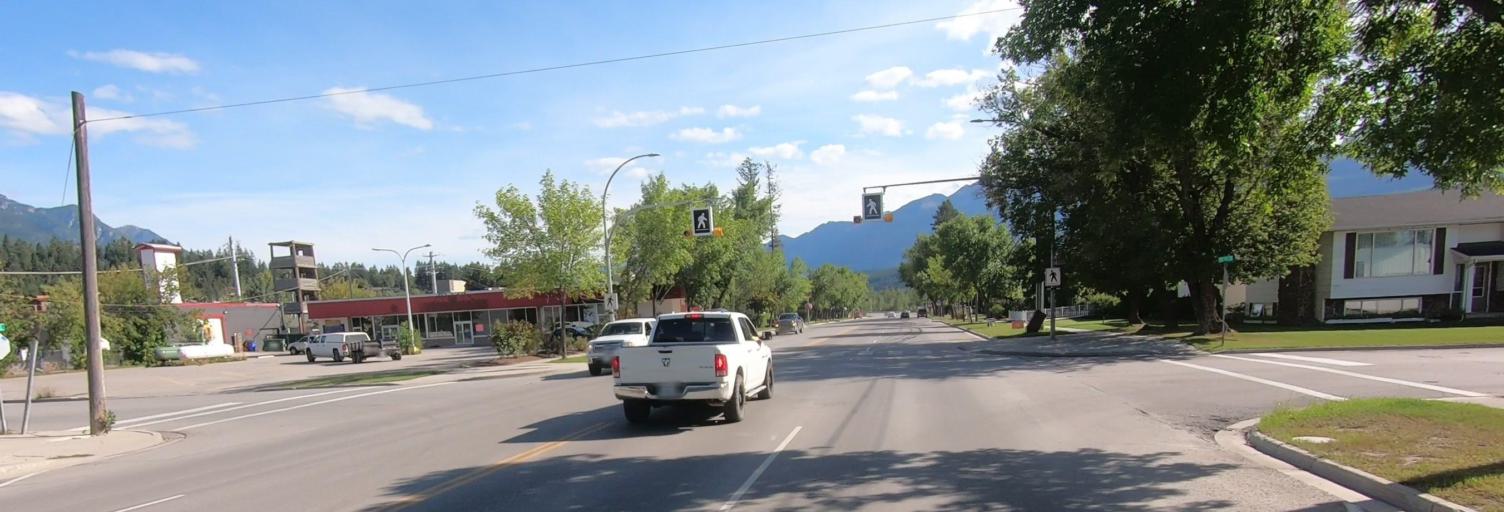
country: CA
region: British Columbia
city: Golden
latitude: 51.2944
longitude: -116.9631
